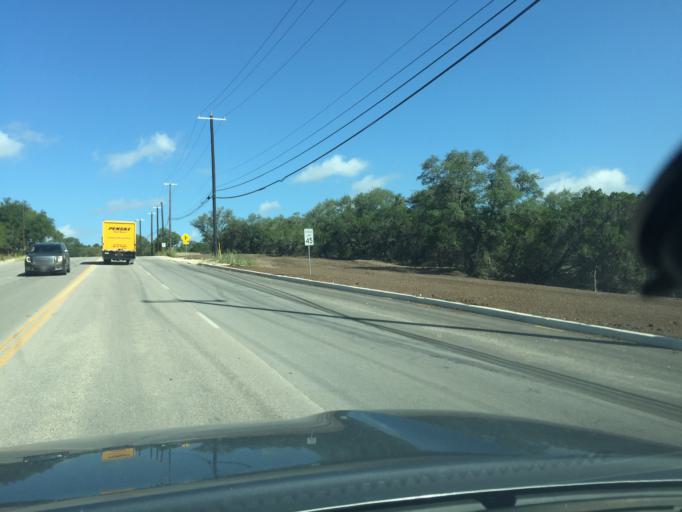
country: US
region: Texas
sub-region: Bexar County
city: Timberwood Park
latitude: 29.7144
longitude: -98.4700
